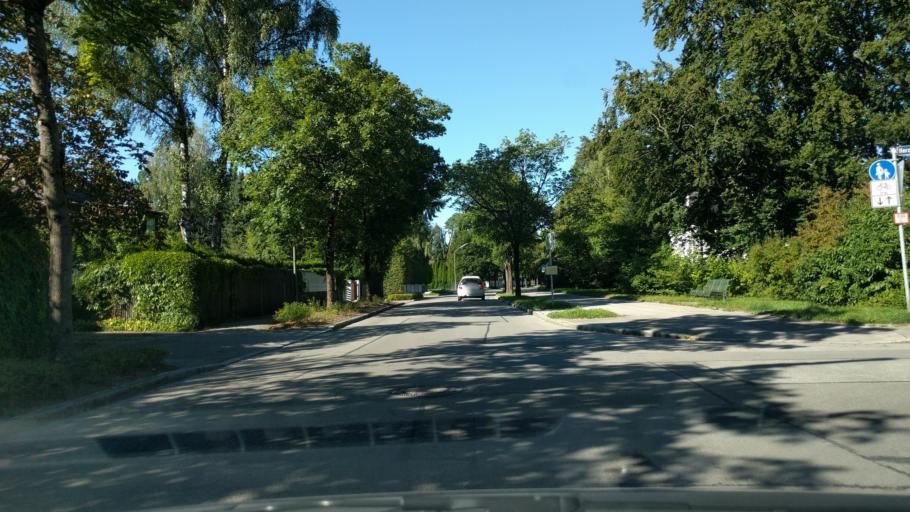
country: DE
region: Bavaria
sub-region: Upper Bavaria
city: Grunwald
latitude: 48.0444
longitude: 11.5386
